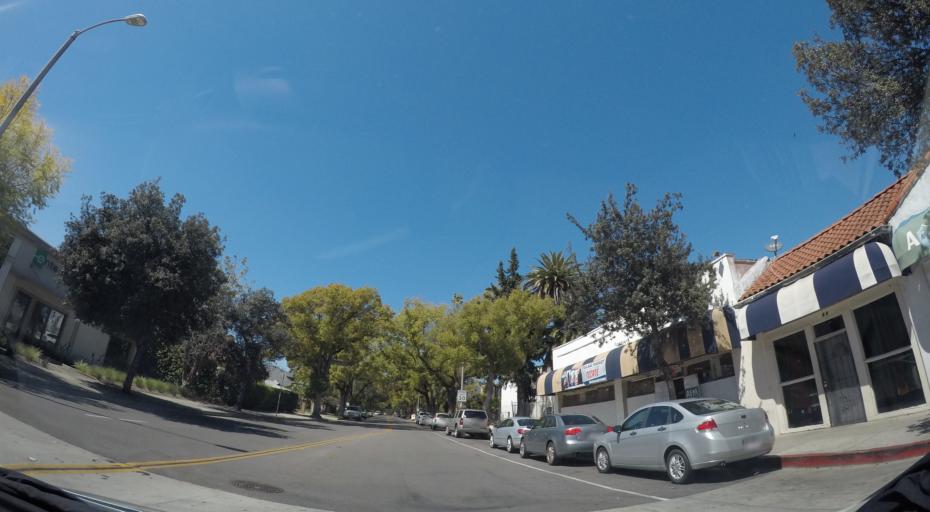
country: US
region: California
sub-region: Los Angeles County
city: Pasadena
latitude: 34.1561
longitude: -118.1550
